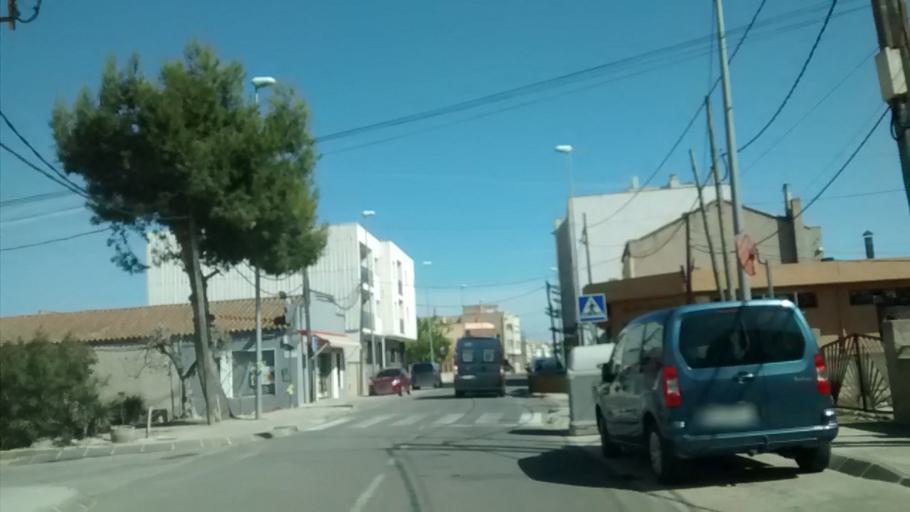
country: ES
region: Catalonia
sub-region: Provincia de Tarragona
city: Deltebre
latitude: 40.7160
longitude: 0.7442
